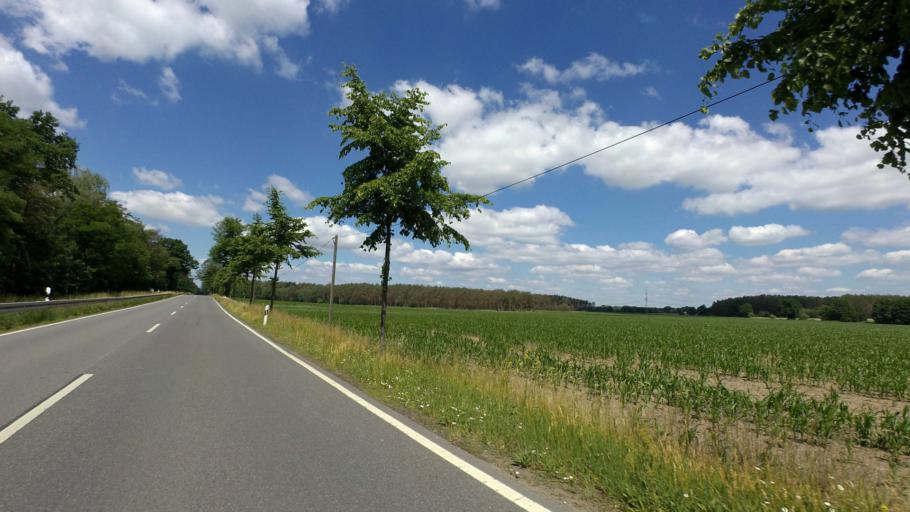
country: DE
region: Brandenburg
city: Finsterwalde
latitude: 51.6501
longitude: 13.6832
